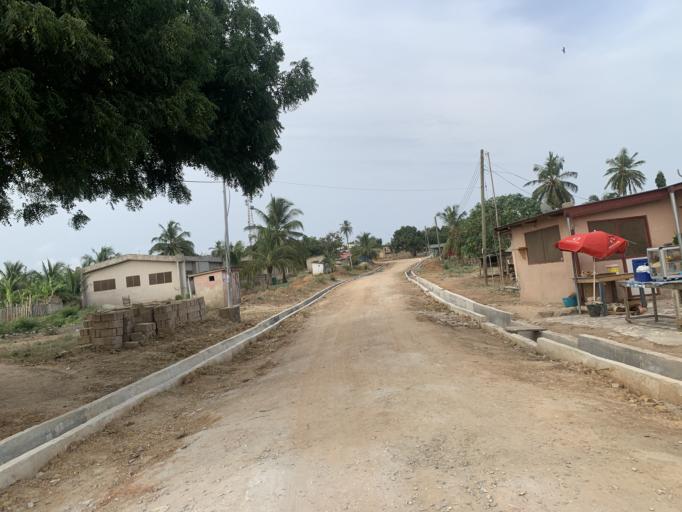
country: GH
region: Central
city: Winneba
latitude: 5.3560
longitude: -0.6279
